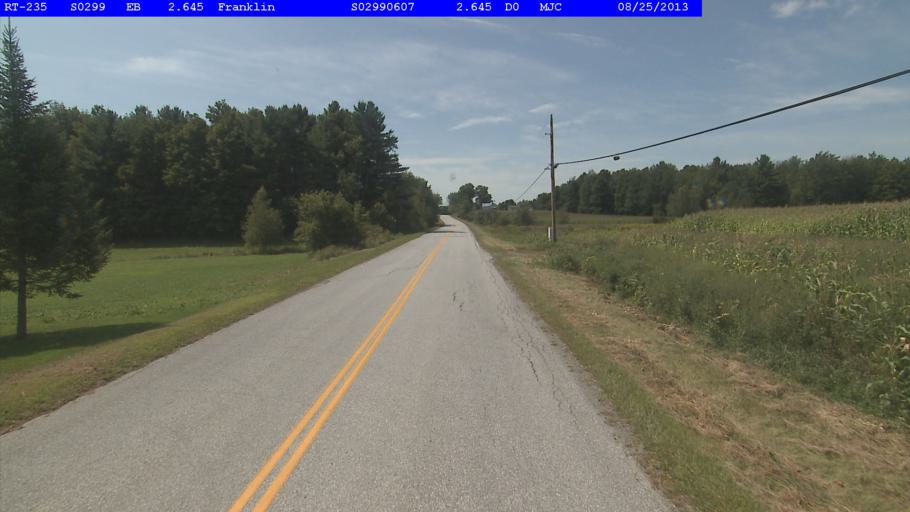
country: CA
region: Quebec
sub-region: Monteregie
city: Bedford
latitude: 45.0023
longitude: -72.9527
